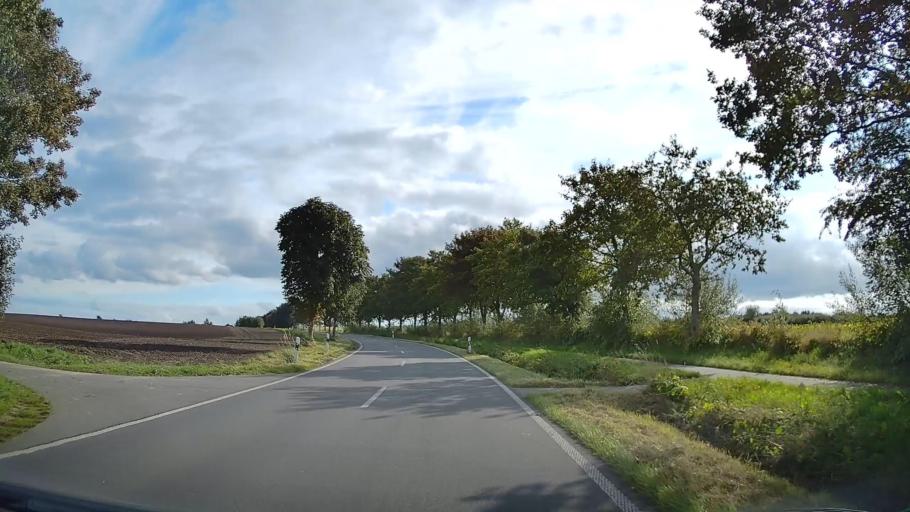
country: DE
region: Schleswig-Holstein
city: Ringsberg
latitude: 54.8137
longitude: 9.5914
